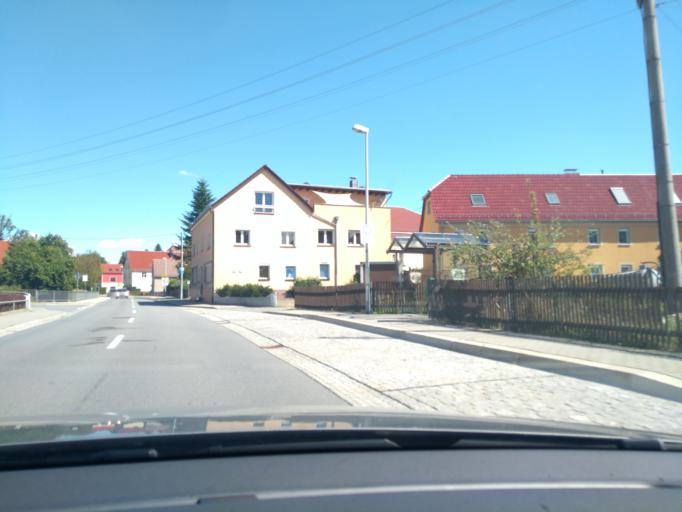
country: DE
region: Saxony
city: Grossrohrsdorf
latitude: 51.1417
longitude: 14.0128
